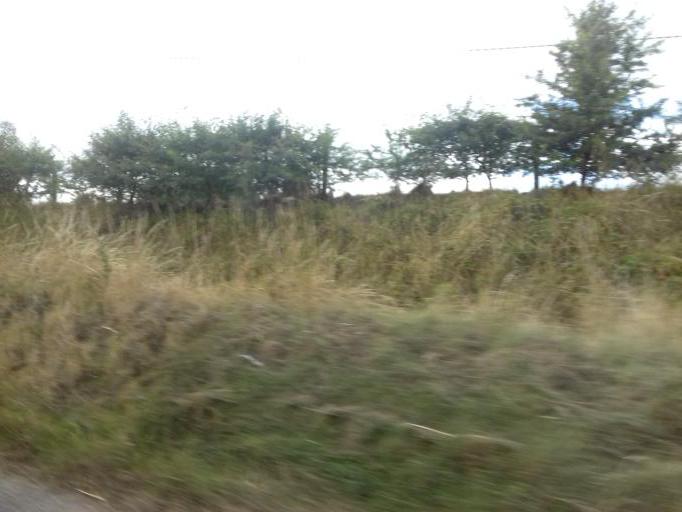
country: IE
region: Leinster
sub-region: County Carlow
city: Tullow
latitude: 52.7877
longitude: -6.7546
